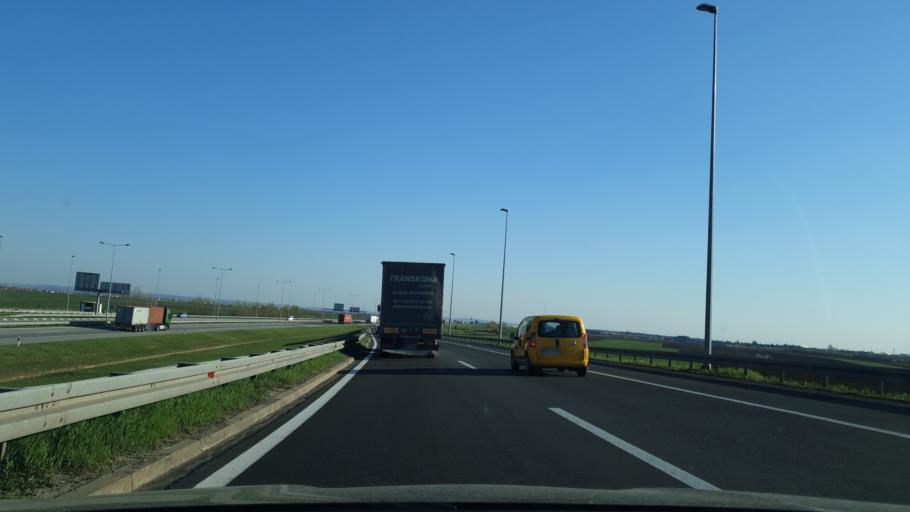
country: RS
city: Dobanovci
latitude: 44.8280
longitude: 20.2507
